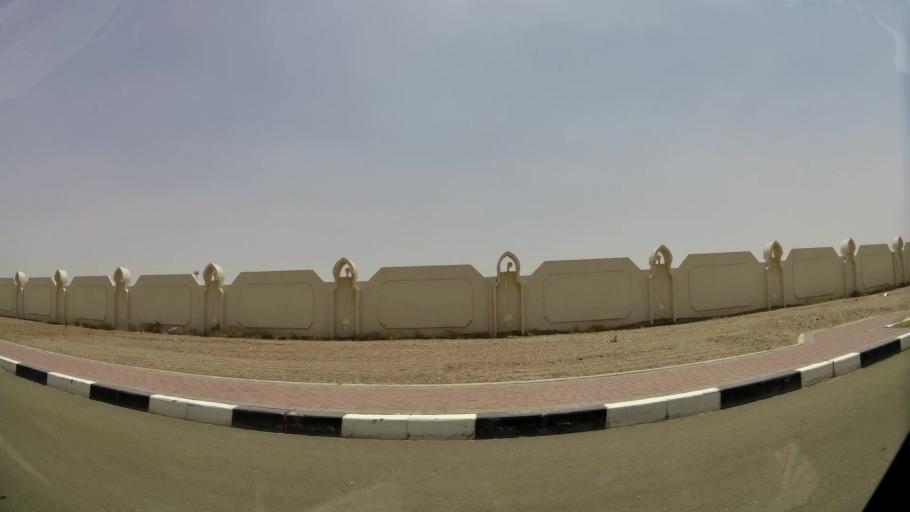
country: AE
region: Abu Dhabi
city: Al Ain
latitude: 24.1941
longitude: 55.6881
